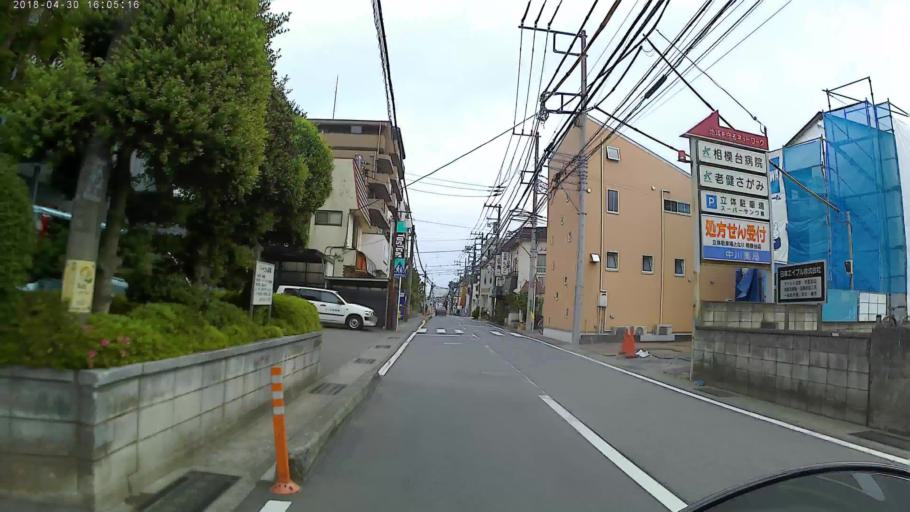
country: JP
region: Kanagawa
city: Minami-rinkan
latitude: 35.5057
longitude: 139.4262
